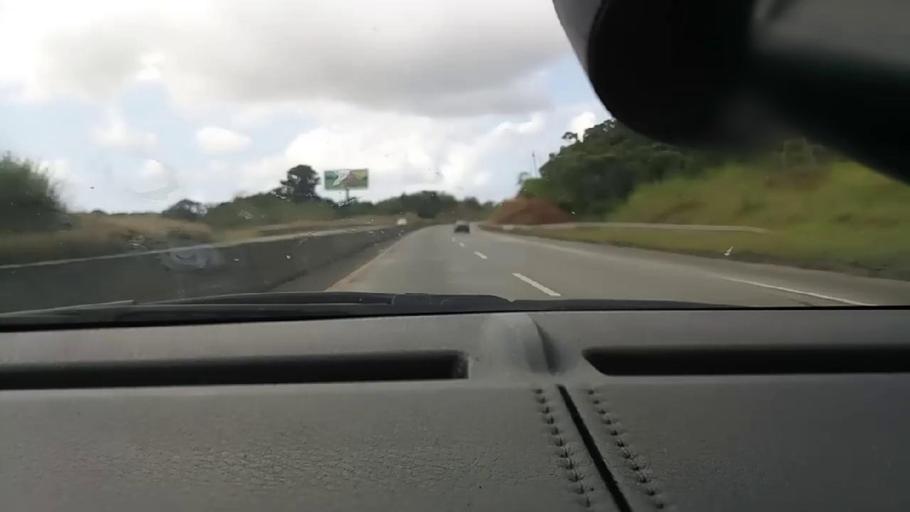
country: PA
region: Colon
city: Gatun
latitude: 9.2817
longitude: -79.7523
